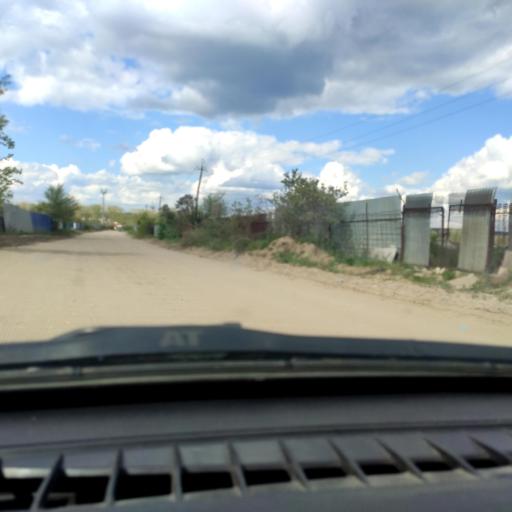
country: RU
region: Samara
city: Zhigulevsk
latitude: 53.4528
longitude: 49.5346
